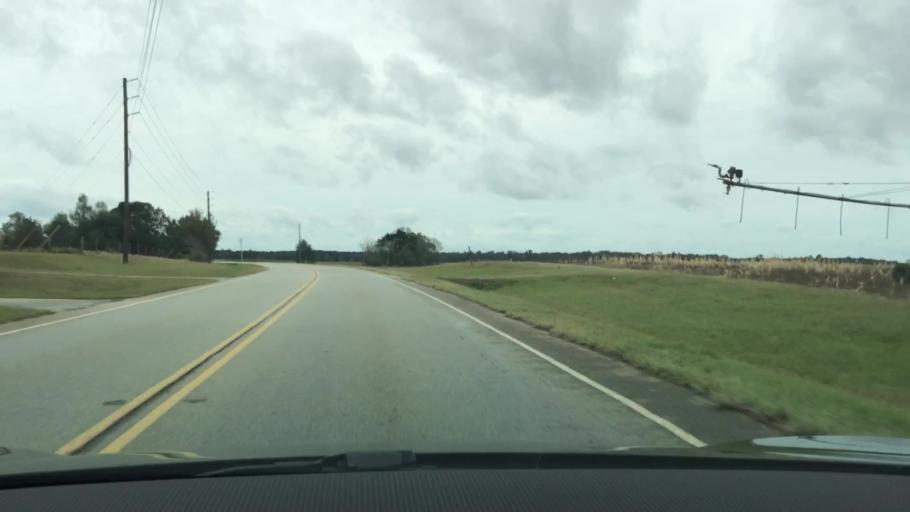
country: US
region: Georgia
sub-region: Jefferson County
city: Wrens
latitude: 33.1524
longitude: -82.4571
